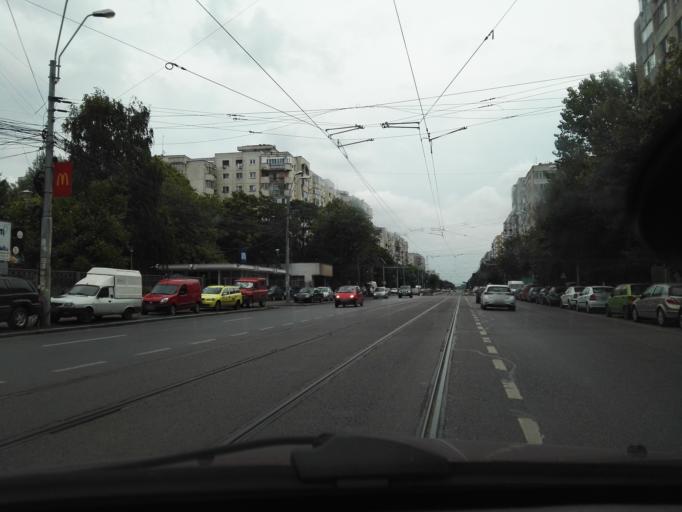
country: RO
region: Ilfov
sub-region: Comuna Popesti-Leordeni
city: Popesti-Leordeni
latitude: 44.3919
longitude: 26.1256
